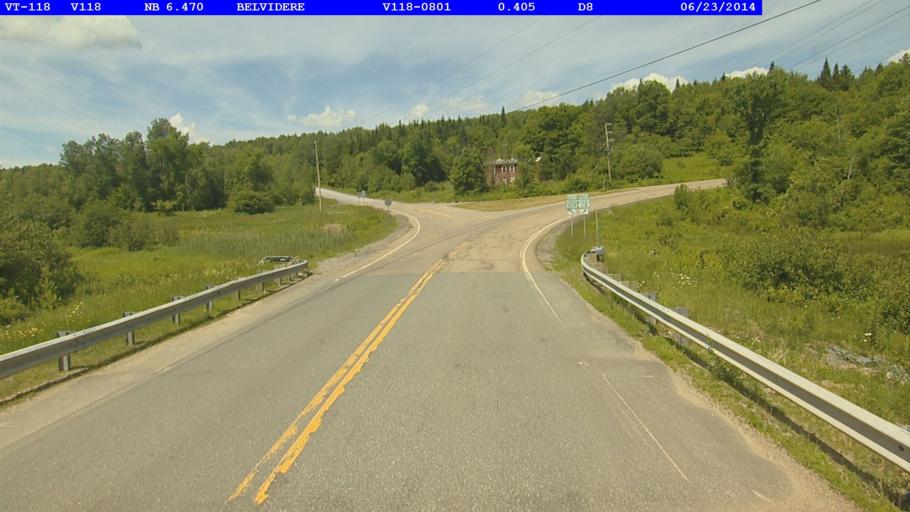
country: US
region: Vermont
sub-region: Lamoille County
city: Johnson
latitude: 44.7661
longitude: -72.6230
